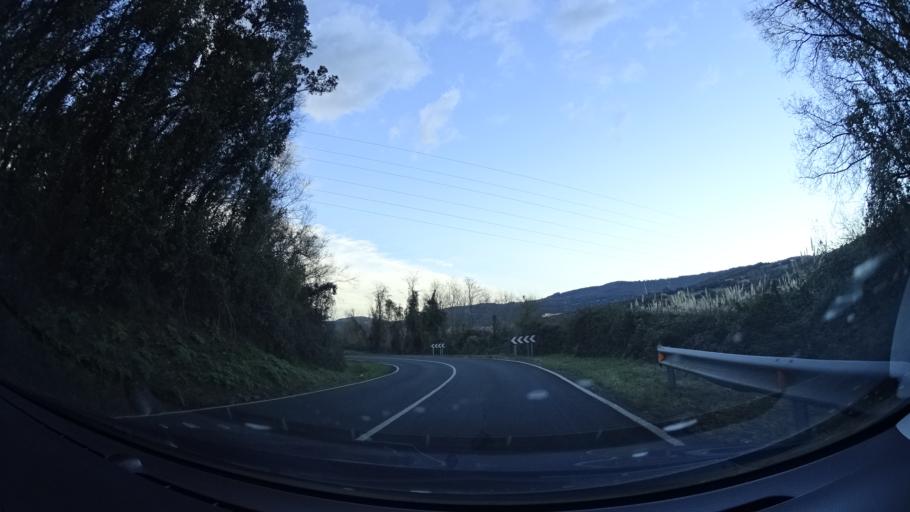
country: ES
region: Basque Country
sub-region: Bizkaia
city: Elexalde
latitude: 43.4036
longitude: -2.9280
